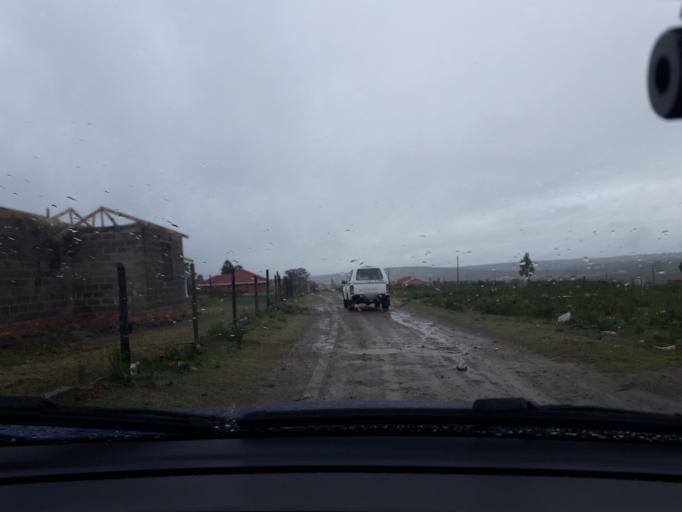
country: ZA
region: Eastern Cape
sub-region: Buffalo City Metropolitan Municipality
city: Bhisho
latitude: -32.8116
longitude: 27.3650
